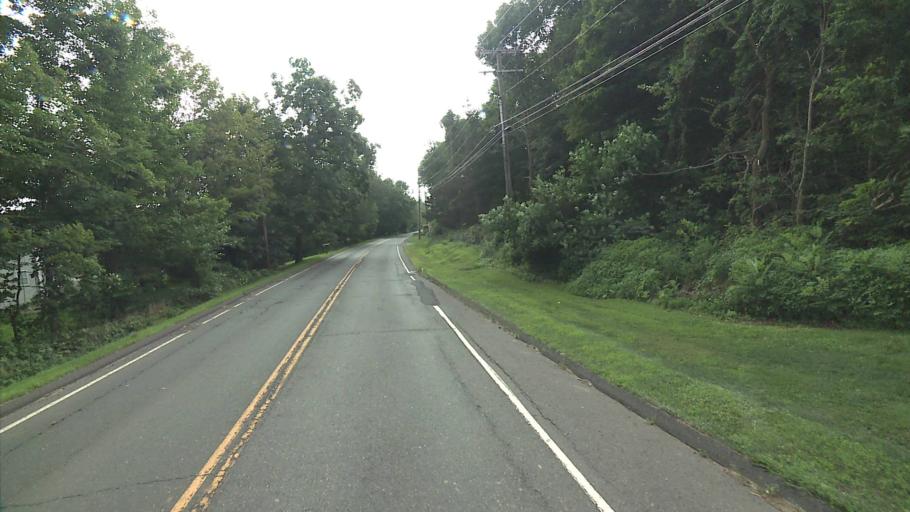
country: US
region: Connecticut
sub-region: New Haven County
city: Oxford
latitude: 41.4552
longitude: -73.1487
